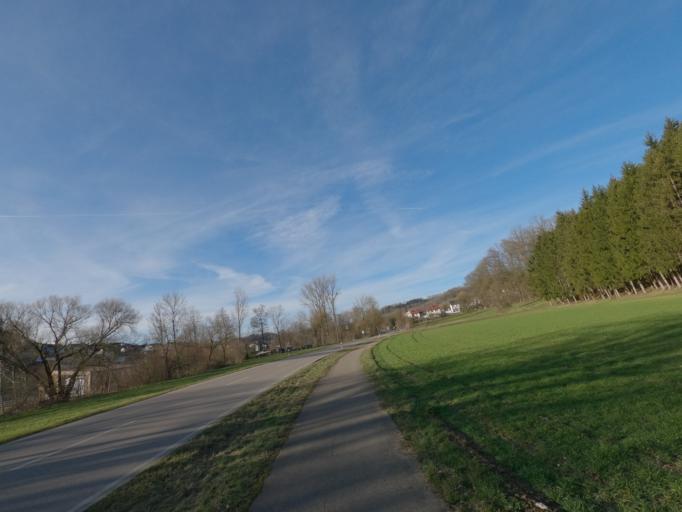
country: DE
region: Baden-Wuerttemberg
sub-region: Regierungsbezirk Stuttgart
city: Donzdorf
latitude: 48.7032
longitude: 9.7985
